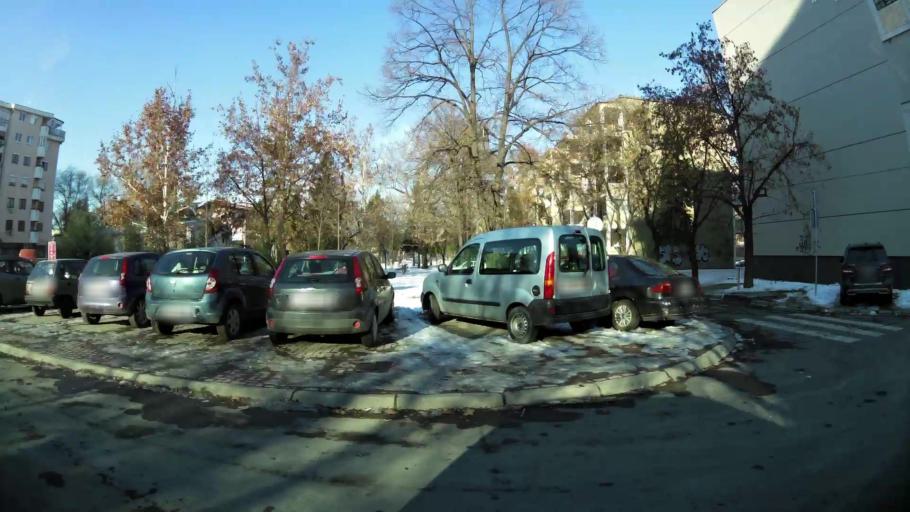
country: MK
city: Krushopek
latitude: 42.0060
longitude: 21.3836
